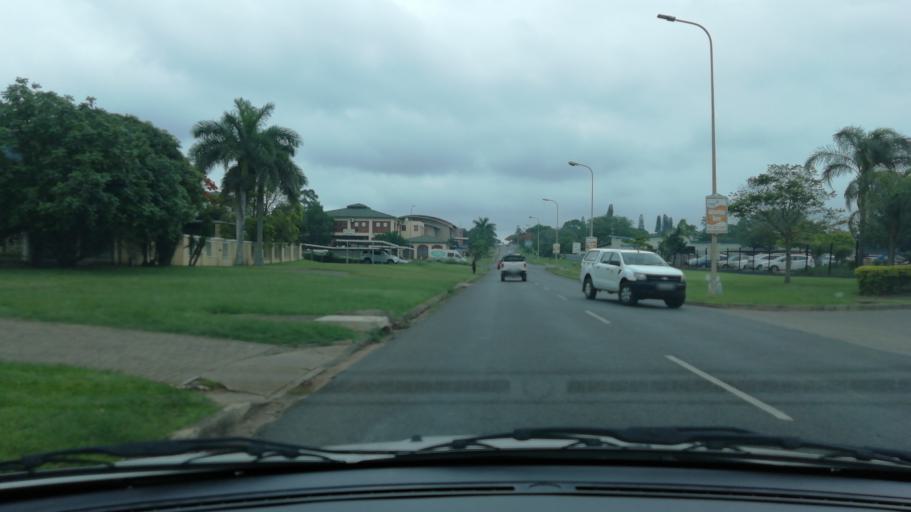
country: ZA
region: KwaZulu-Natal
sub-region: uThungulu District Municipality
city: Empangeni
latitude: -28.7363
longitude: 31.8940
